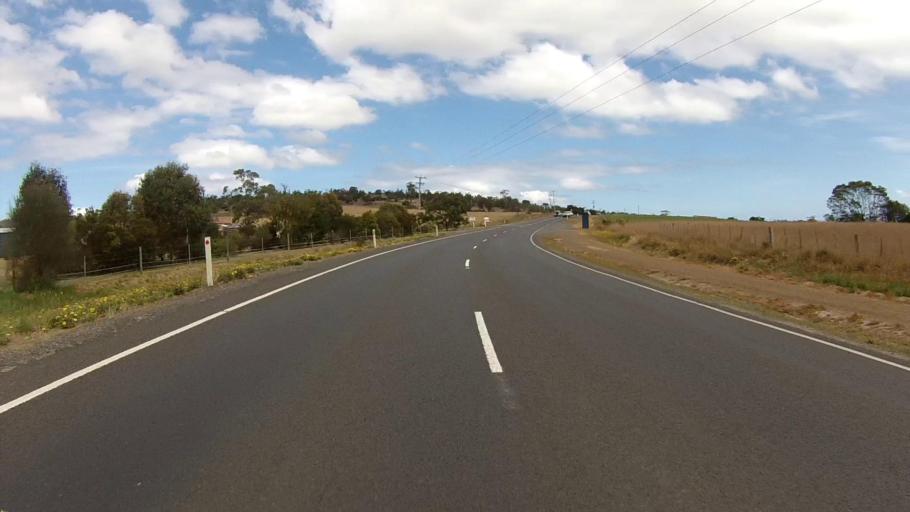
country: AU
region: Tasmania
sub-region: Sorell
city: Sorell
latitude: -42.8323
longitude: 147.6245
